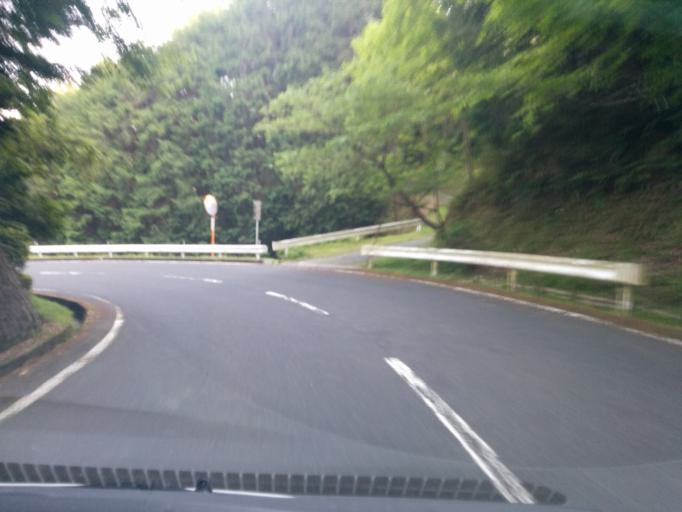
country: JP
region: Shiga Prefecture
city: Kitahama
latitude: 35.1026
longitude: 135.8609
